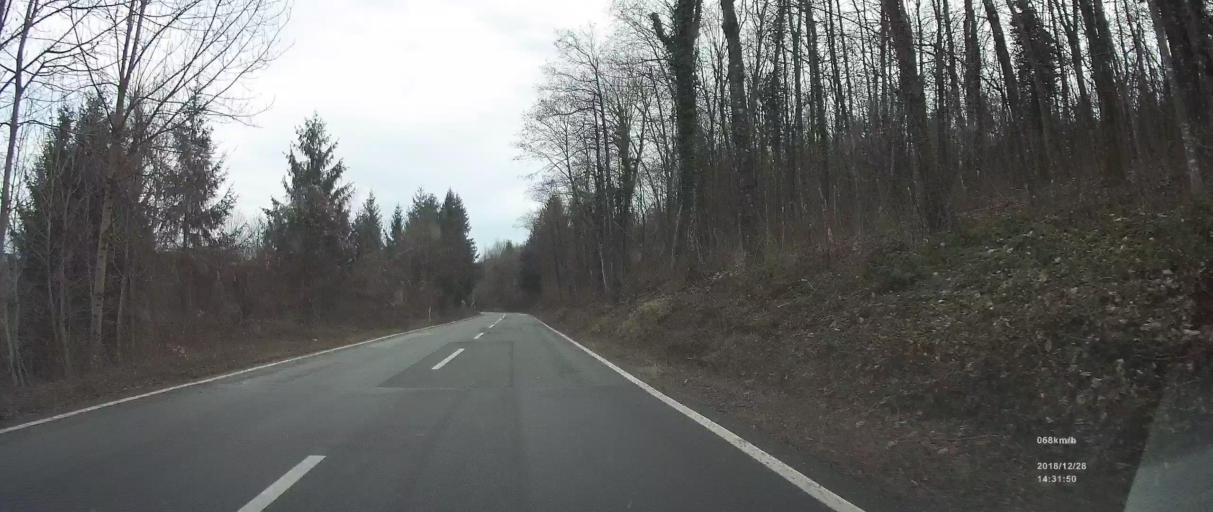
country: HR
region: Primorsko-Goranska
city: Vrbovsko
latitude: 45.4149
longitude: 15.1479
